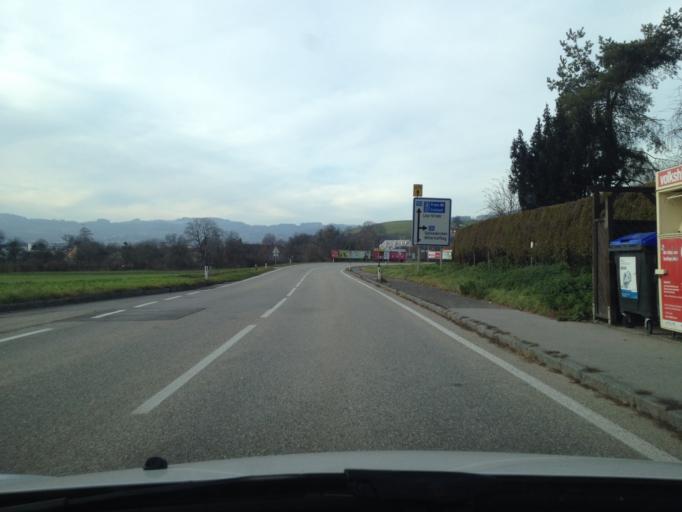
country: AT
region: Upper Austria
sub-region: Politischer Bezirk Urfahr-Umgebung
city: Altenberg bei Linz
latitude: 48.3265
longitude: 14.3376
